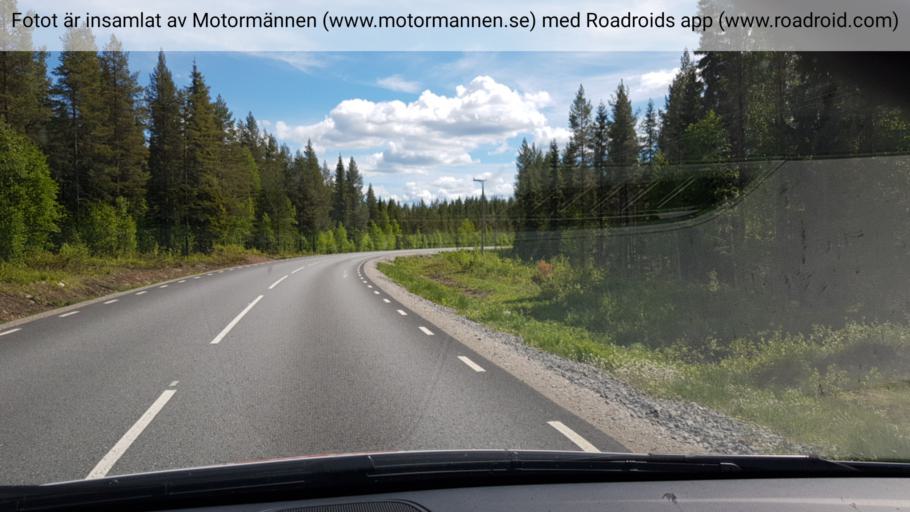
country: SE
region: Vaesterbotten
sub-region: Skelleftea Kommun
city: Langsele
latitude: 64.7511
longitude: 20.3459
